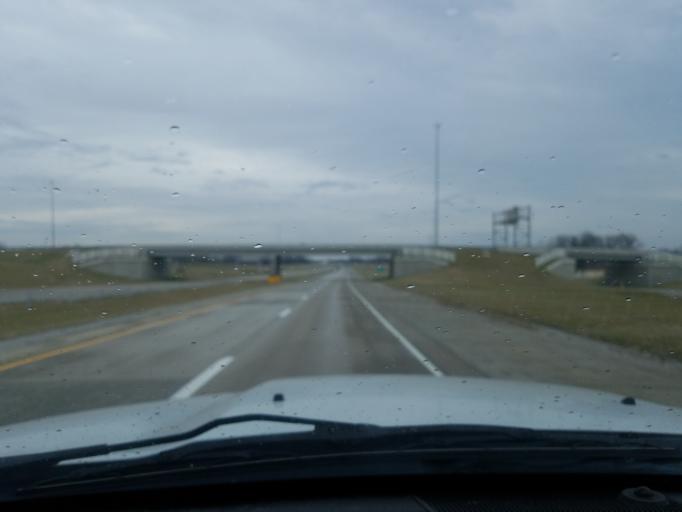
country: US
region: Indiana
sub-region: Clark County
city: Oak Park
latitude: 38.3438
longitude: -85.7015
